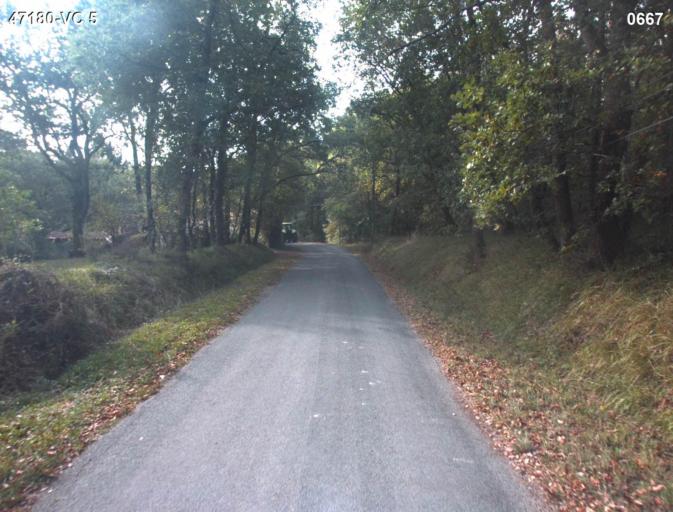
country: FR
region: Aquitaine
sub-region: Departement du Lot-et-Garonne
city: Sainte-Colombe-en-Bruilhois
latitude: 44.1770
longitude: 0.4678
